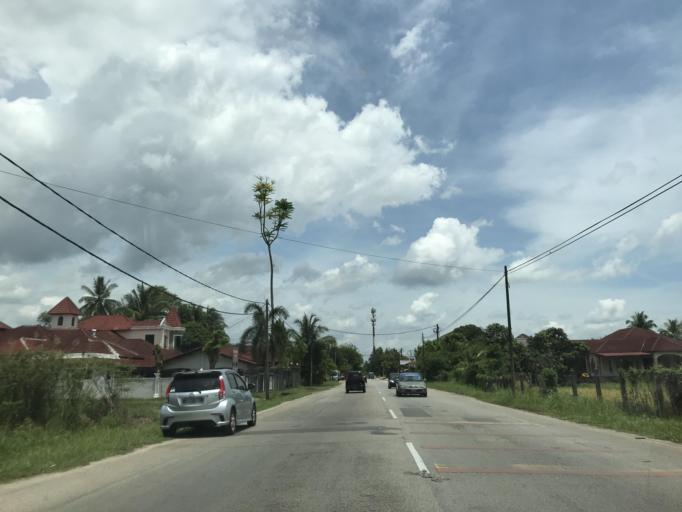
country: MY
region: Kelantan
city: Pasir Mas
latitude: 6.0511
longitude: 102.1846
